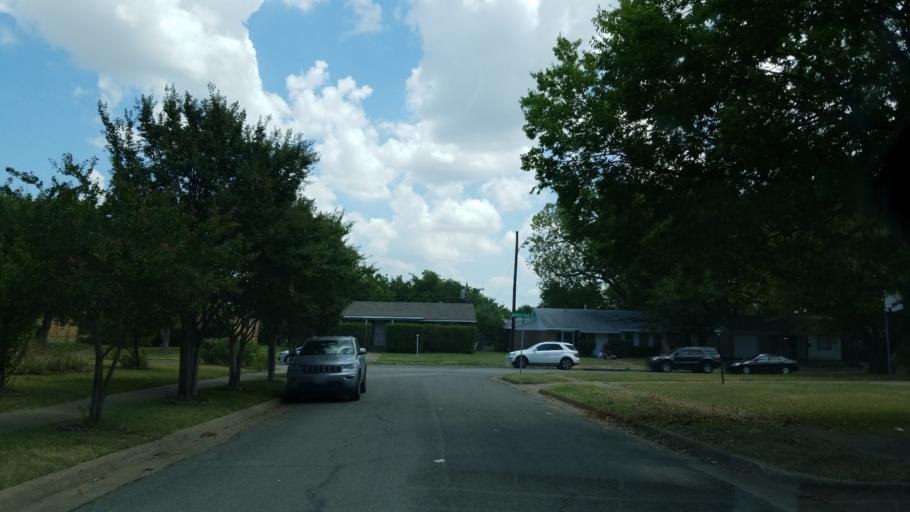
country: US
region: Texas
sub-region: Dallas County
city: Cockrell Hill
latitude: 32.7261
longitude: -96.8982
